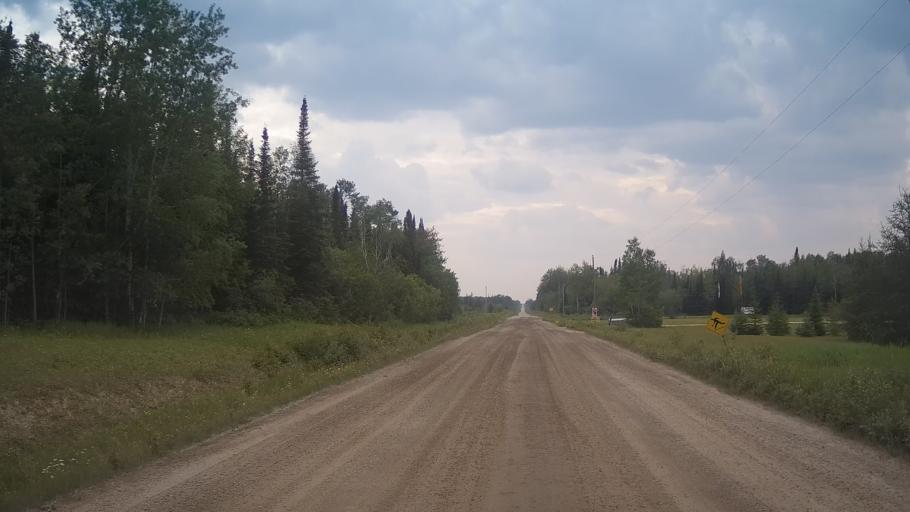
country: CA
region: Ontario
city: Hearst
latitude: 49.6449
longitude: -83.2825
